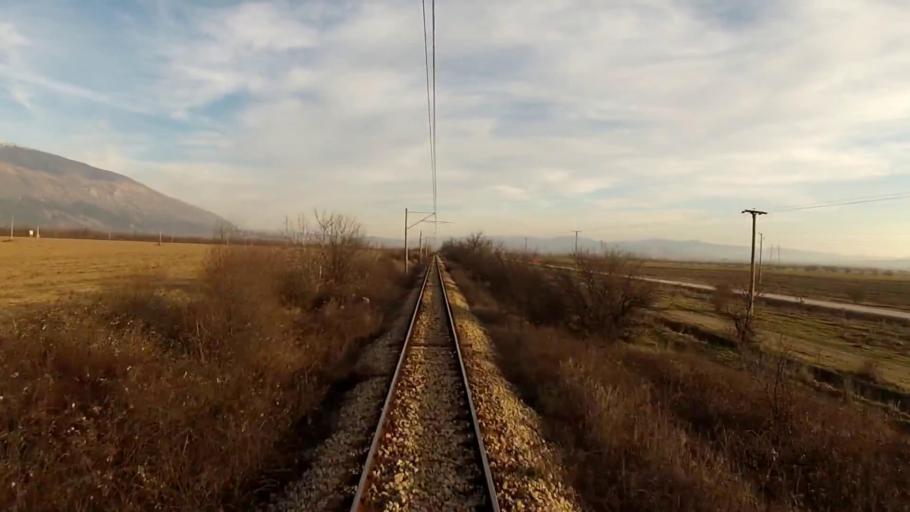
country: BG
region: Plovdiv
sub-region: Obshtina Karlovo
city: Karlovo
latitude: 42.6338
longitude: 24.7710
